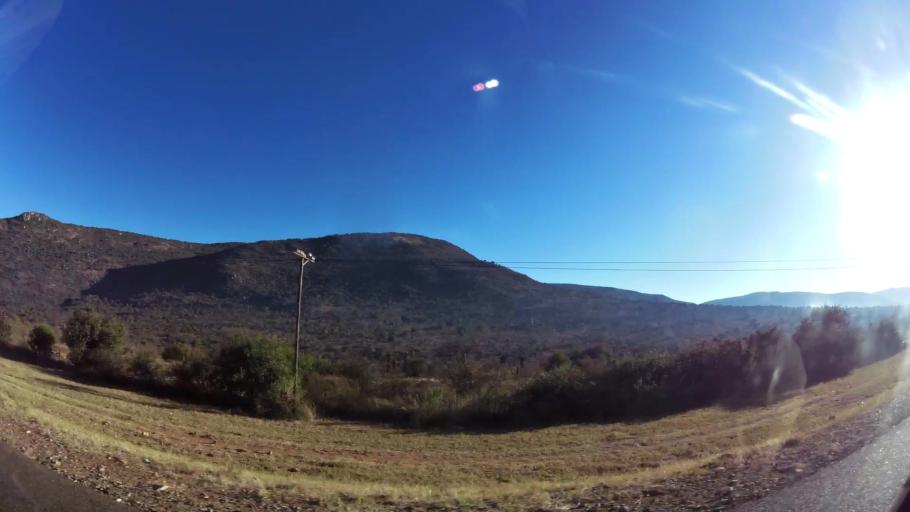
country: ZA
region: Limpopo
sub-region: Capricorn District Municipality
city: Mankoeng
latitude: -23.9435
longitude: 29.8171
